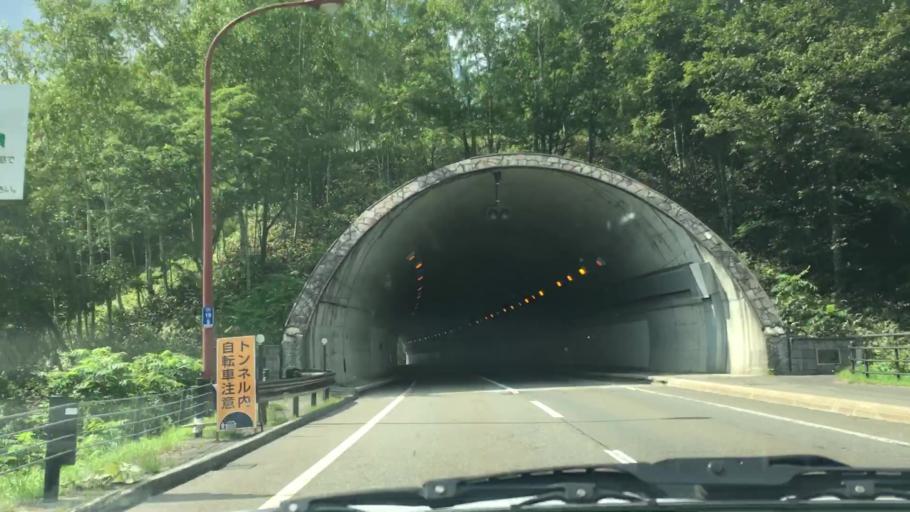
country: JP
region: Hokkaido
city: Otofuke
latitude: 43.3705
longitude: 143.2275
